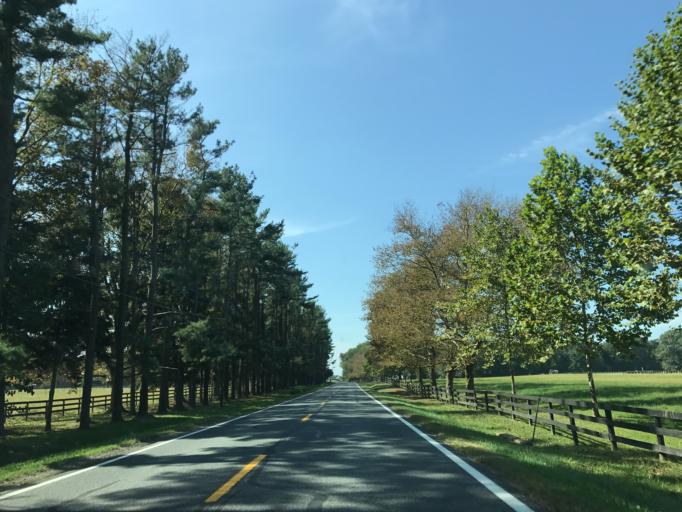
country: US
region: Maryland
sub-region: Cecil County
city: Elkton
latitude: 39.4908
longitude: -75.8265
